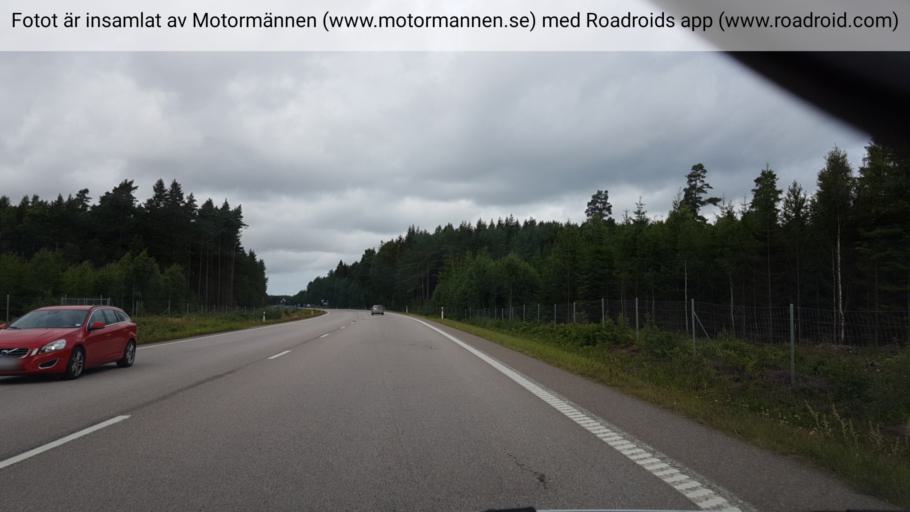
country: SE
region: Vaestra Goetaland
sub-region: Lidkopings Kommun
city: Lidkoping
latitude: 58.4797
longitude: 13.2016
